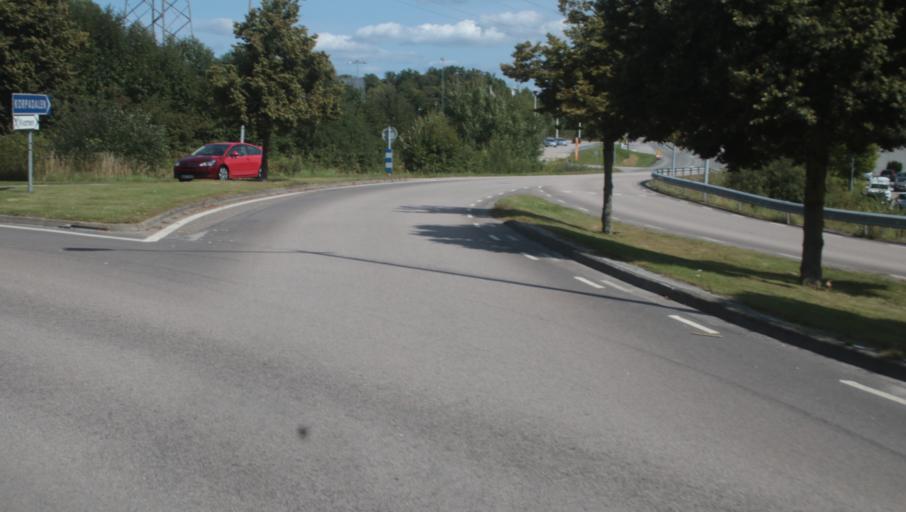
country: SE
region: Blekinge
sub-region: Karlshamns Kommun
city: Karlshamn
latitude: 56.1940
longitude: 14.8422
